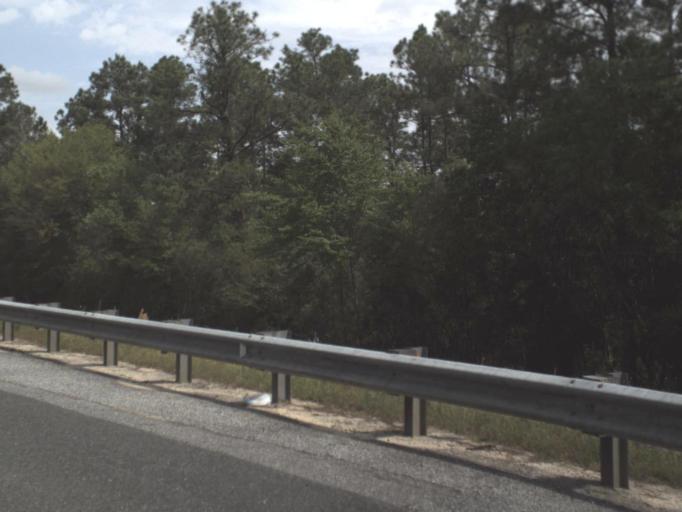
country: US
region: Florida
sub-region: Santa Rosa County
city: East Milton
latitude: 30.5818
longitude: -86.9291
